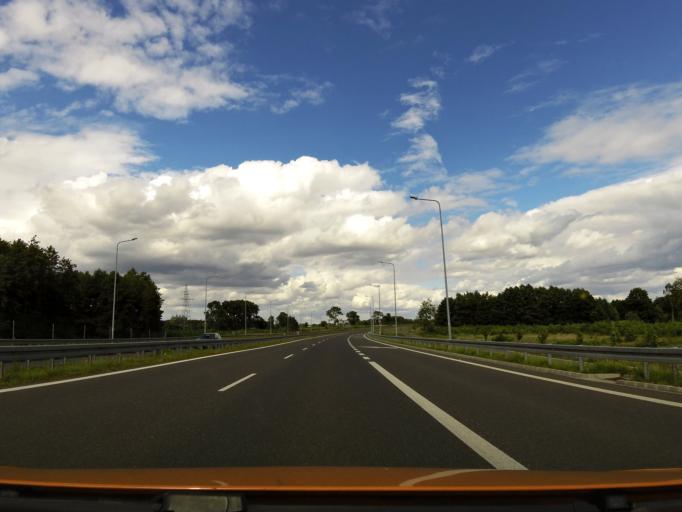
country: PL
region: West Pomeranian Voivodeship
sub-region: Powiat goleniowski
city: Nowogard
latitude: 53.6876
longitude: 15.0908
